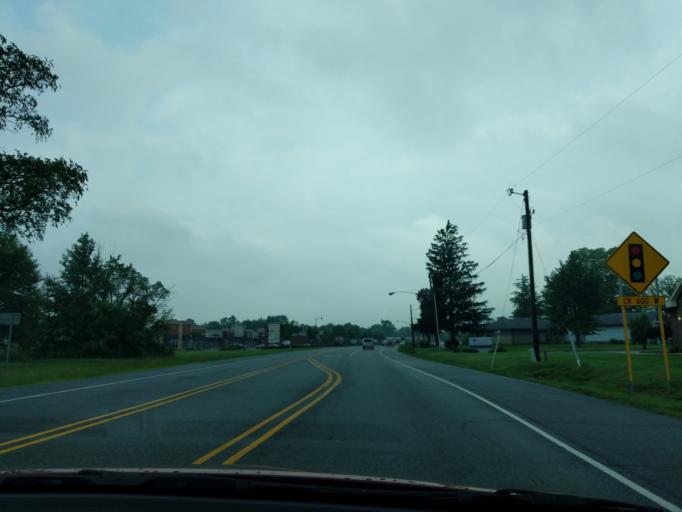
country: US
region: Indiana
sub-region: Hancock County
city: McCordsville
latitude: 39.8979
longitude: -85.9161
